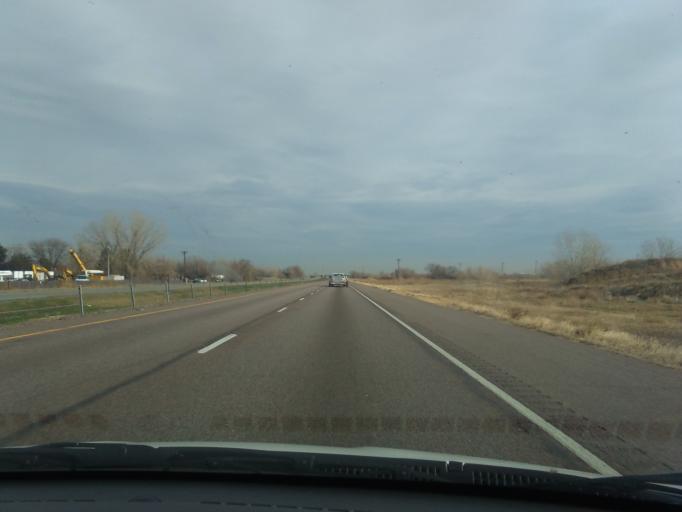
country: US
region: Colorado
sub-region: Adams County
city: Todd Creek
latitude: 39.8982
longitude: -104.8444
